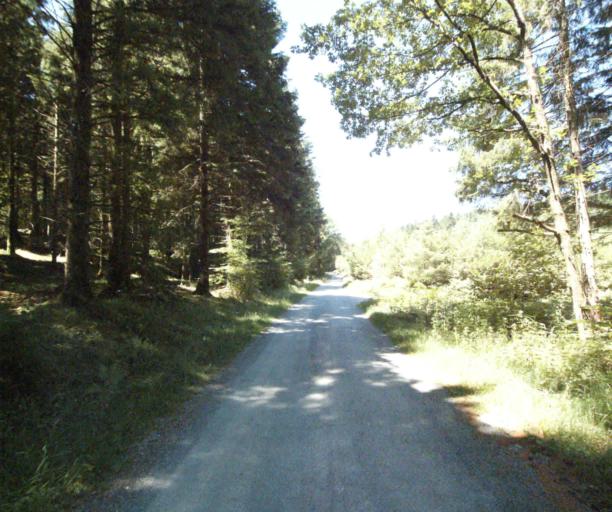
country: FR
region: Languedoc-Roussillon
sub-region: Departement de l'Aude
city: Cuxac-Cabardes
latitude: 43.4024
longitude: 2.2109
